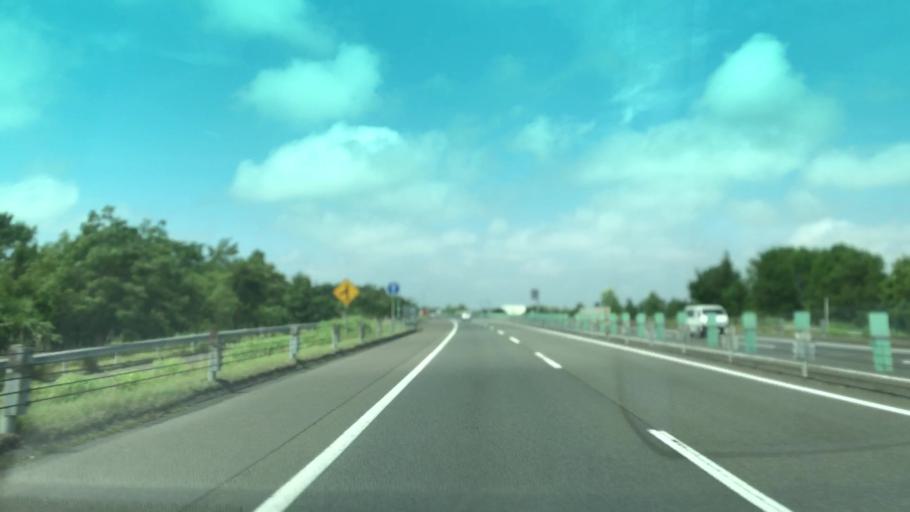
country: JP
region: Hokkaido
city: Kitahiroshima
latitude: 42.9049
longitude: 141.5506
